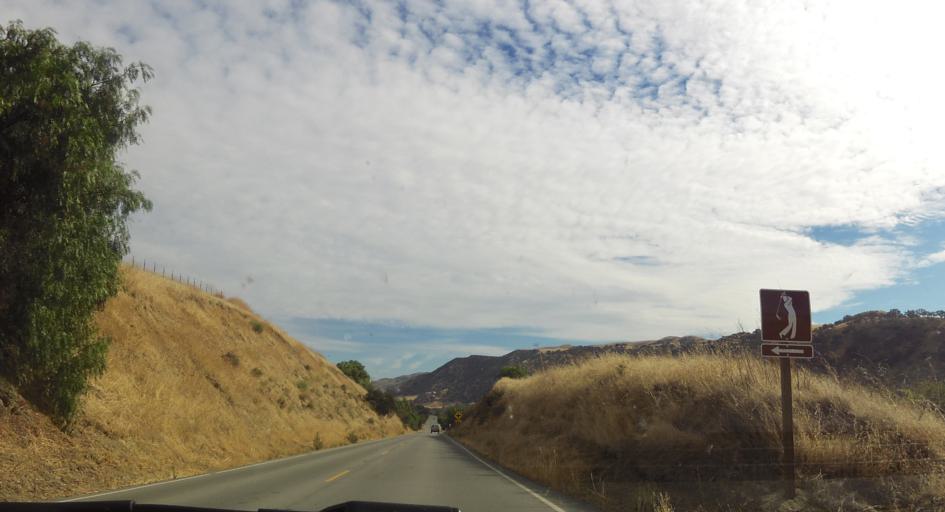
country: US
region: California
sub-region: San Benito County
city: Ridgemark
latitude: 36.7826
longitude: -121.3137
